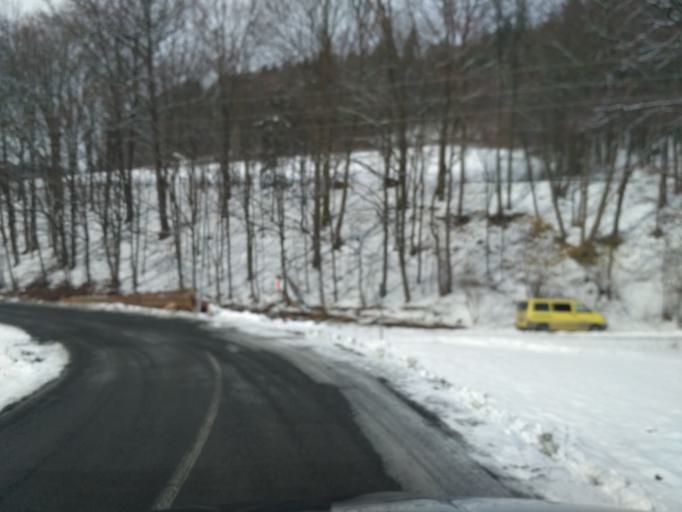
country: CZ
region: Zlin
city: Vidce
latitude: 49.4212
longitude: 18.0768
